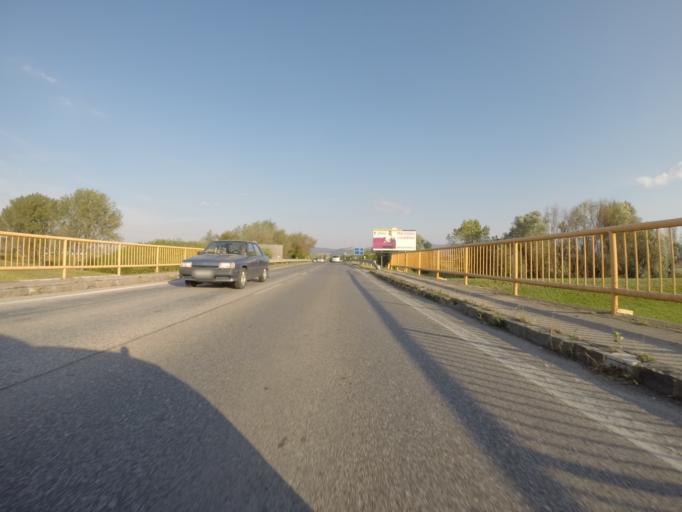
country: SK
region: Nitriansky
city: Banovce nad Bebravou
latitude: 48.5545
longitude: 18.1842
